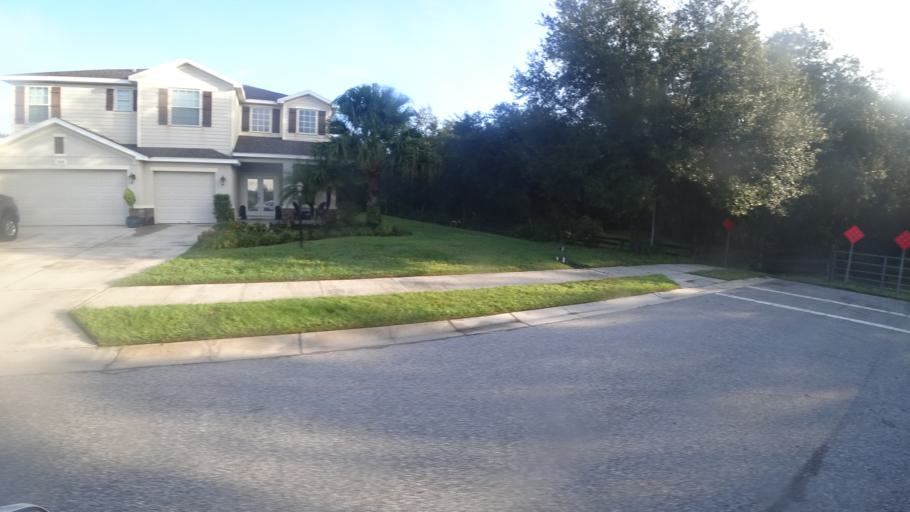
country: US
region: Florida
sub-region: Manatee County
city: Ellenton
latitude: 27.5402
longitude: -82.4111
